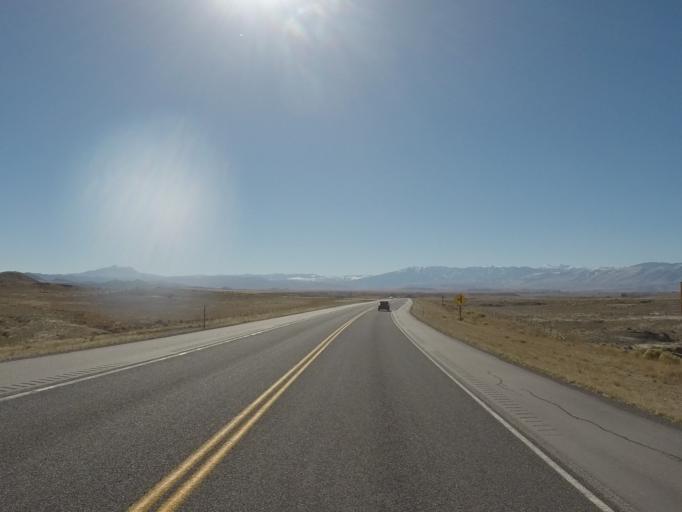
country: US
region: Montana
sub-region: Carbon County
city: Red Lodge
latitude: 44.9046
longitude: -109.1024
